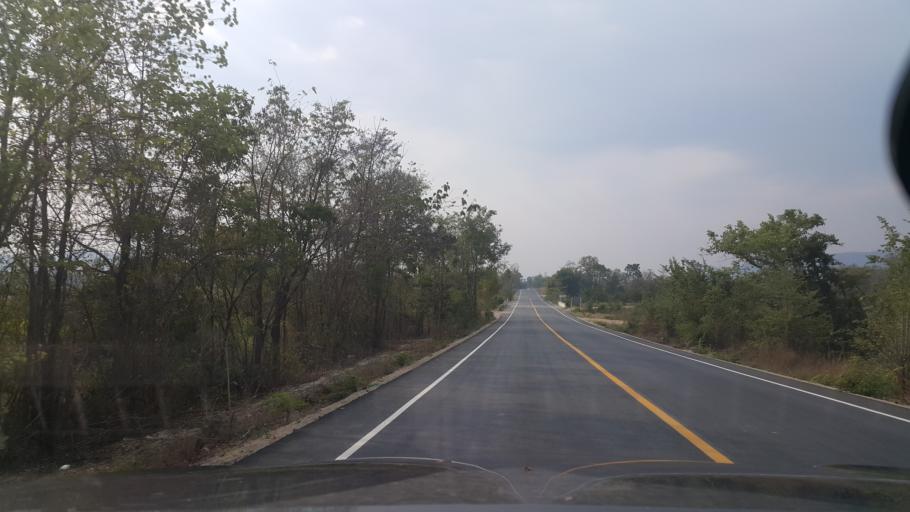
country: TH
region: Sukhothai
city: Thung Saliam
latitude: 17.2422
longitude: 99.5160
